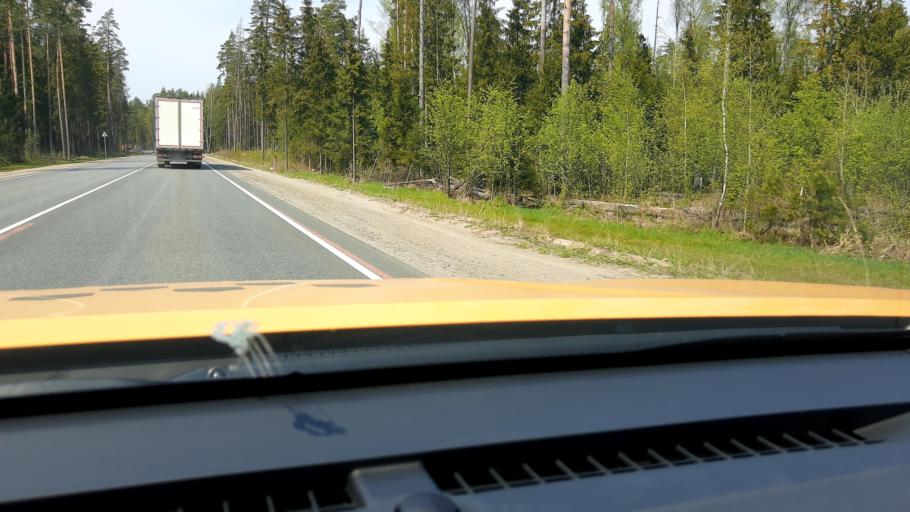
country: RU
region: Moskovskaya
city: Chernogolovka
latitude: 56.0094
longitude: 38.2705
